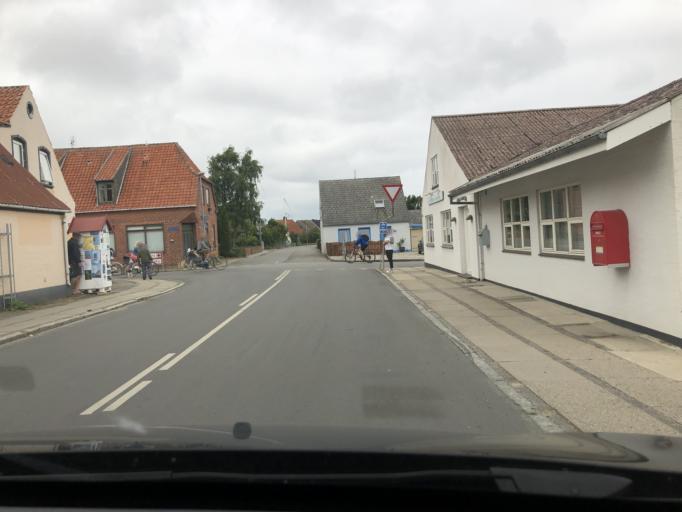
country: DK
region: South Denmark
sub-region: AEro Kommune
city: Marstal
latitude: 54.8558
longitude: 10.5148
